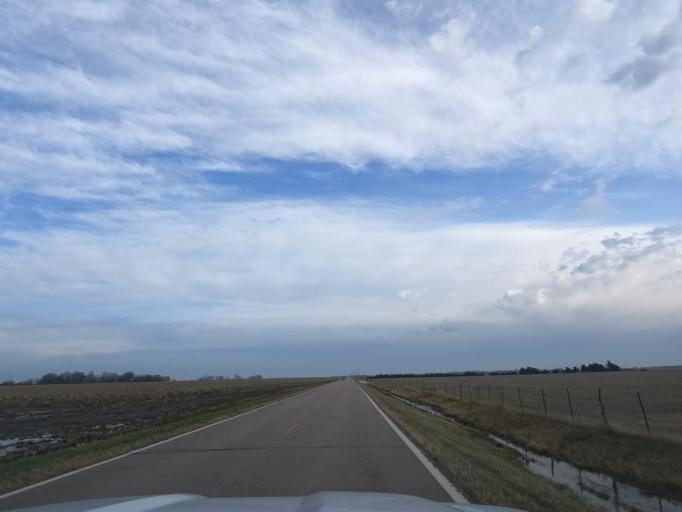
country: US
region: Kansas
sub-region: Reno County
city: Nickerson
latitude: 38.0249
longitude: -98.1786
